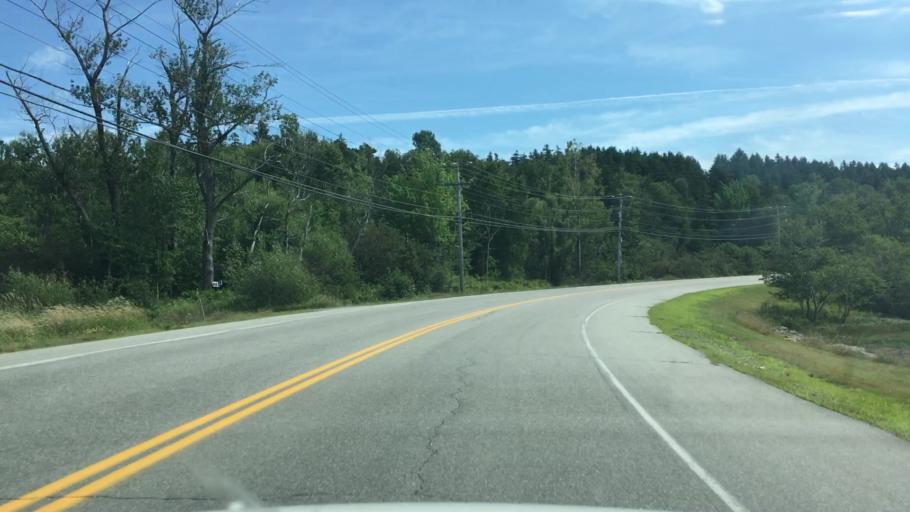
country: US
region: Maine
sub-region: Washington County
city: Eastport
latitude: 44.9236
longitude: -67.0151
